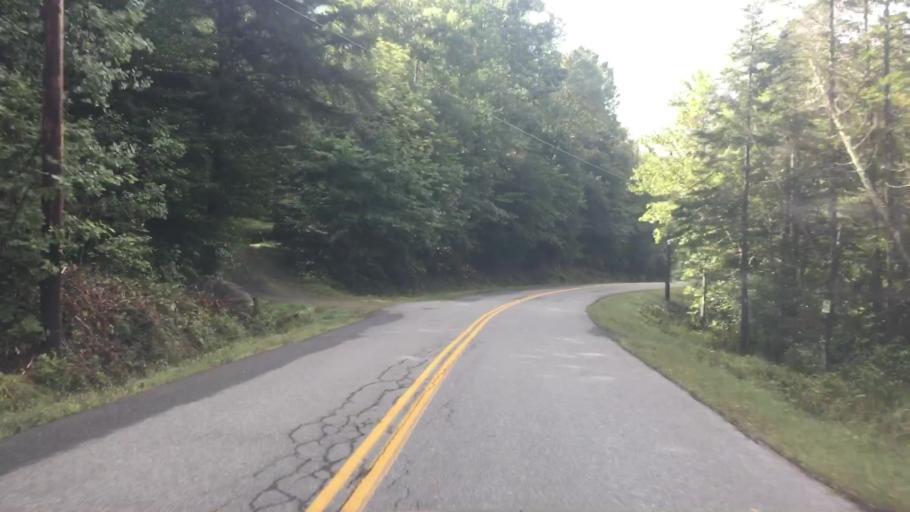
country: US
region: Vermont
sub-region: Windham County
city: Dover
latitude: 42.8084
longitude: -72.7662
